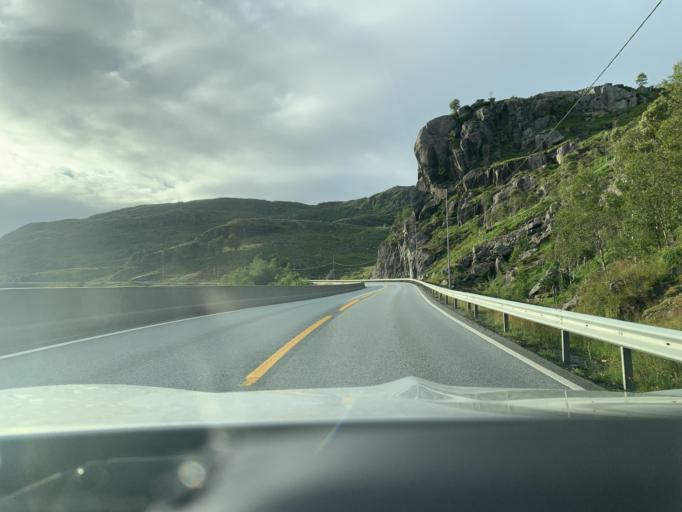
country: NO
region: Rogaland
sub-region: Bjerkreim
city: Vikesa
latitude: 58.6596
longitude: 6.0187
